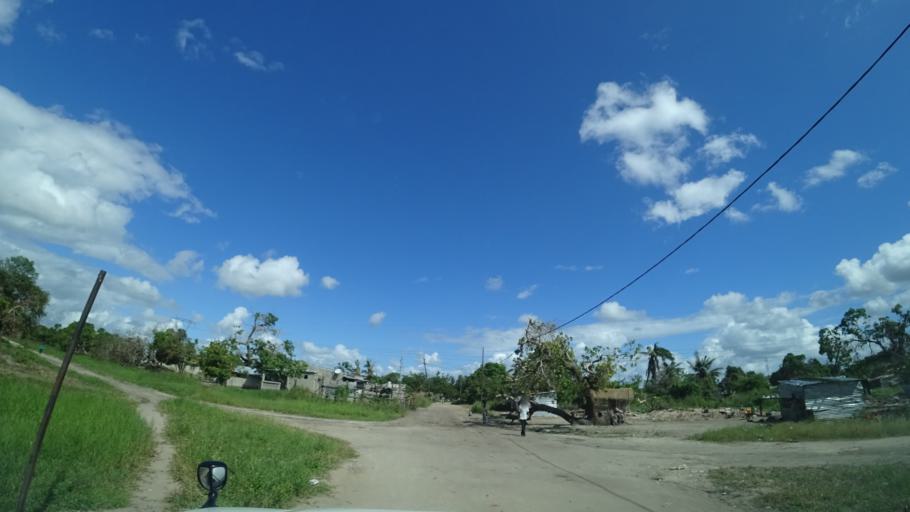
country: MZ
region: Sofala
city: Dondo
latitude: -19.4971
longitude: 34.5984
